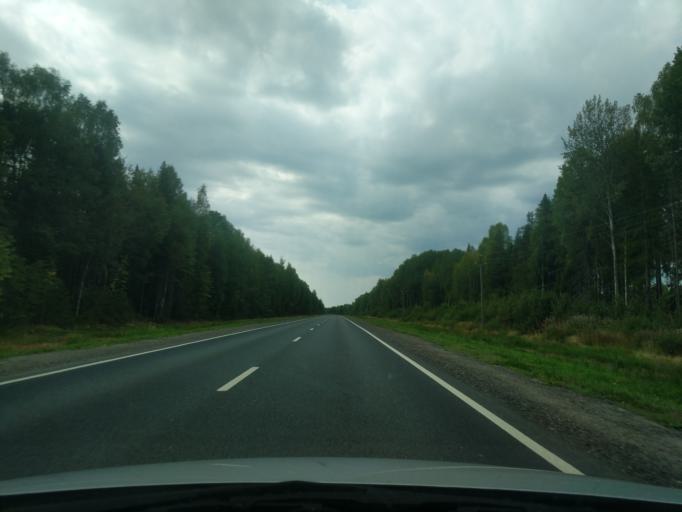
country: RU
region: Kostroma
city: Manturovo
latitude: 58.1589
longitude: 44.3905
